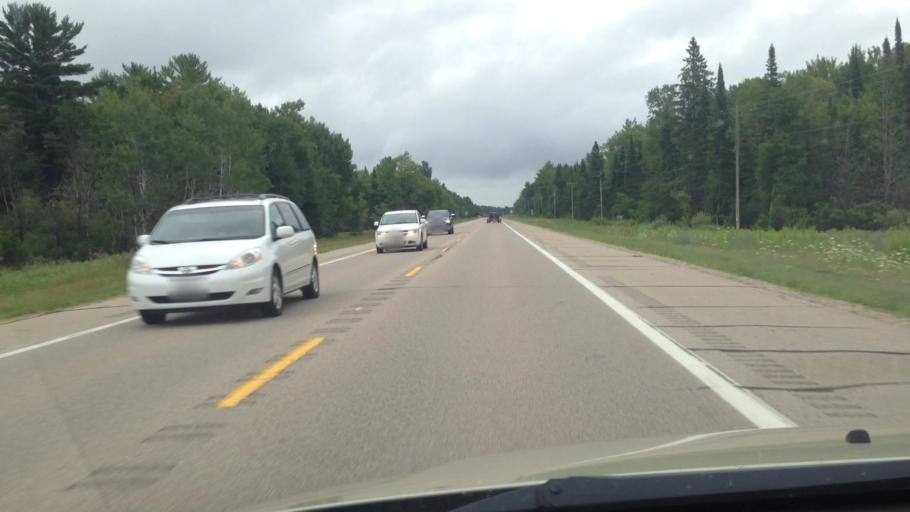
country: US
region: Michigan
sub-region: Delta County
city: Gladstone
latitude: 45.8955
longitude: -86.7220
